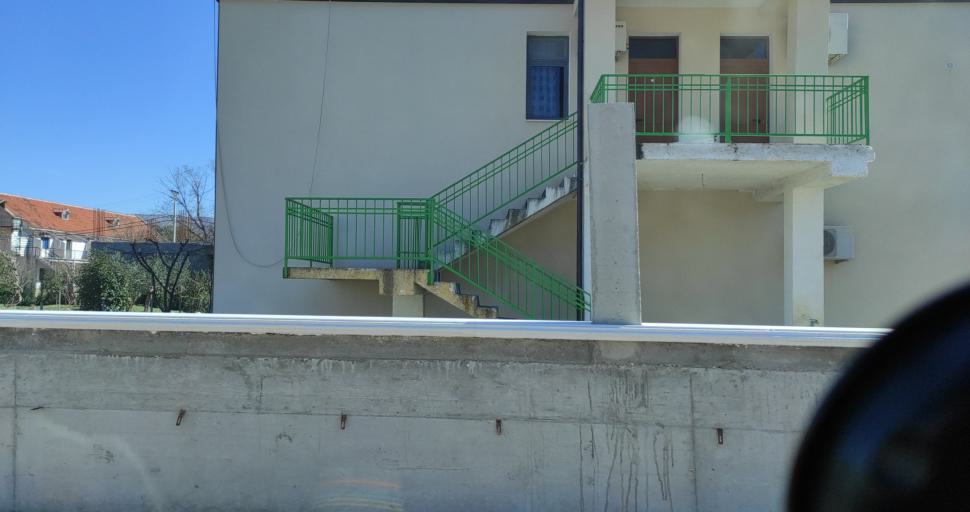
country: AL
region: Shkoder
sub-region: Rrethi i Shkodres
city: Velipoje
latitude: 41.8642
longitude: 19.4120
